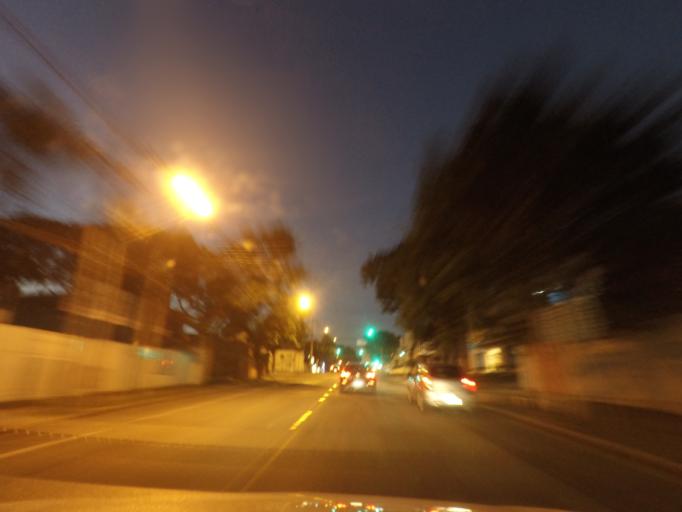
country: BR
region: Parana
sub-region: Curitiba
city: Curitiba
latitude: -25.4544
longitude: -49.2771
